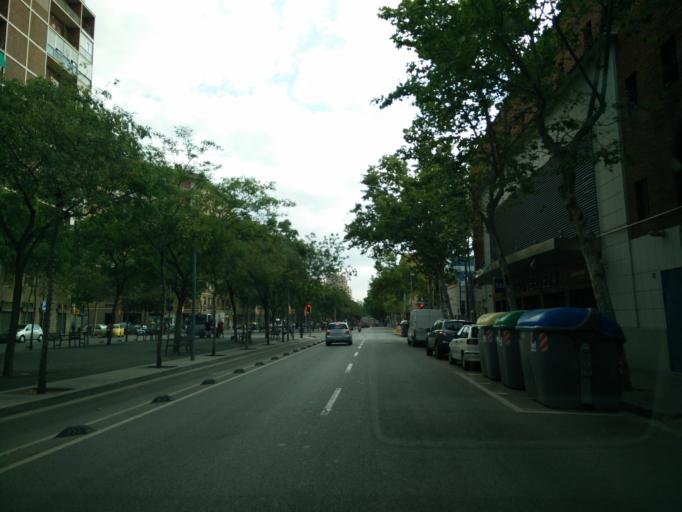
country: ES
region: Catalonia
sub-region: Provincia de Barcelona
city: Sant Marti
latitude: 41.4165
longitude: 2.1977
